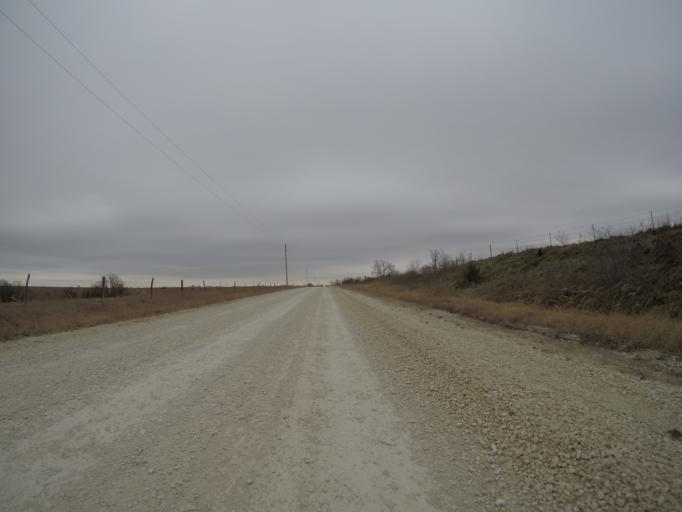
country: US
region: Kansas
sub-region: Wabaunsee County
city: Alma
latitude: 38.8352
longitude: -96.1133
